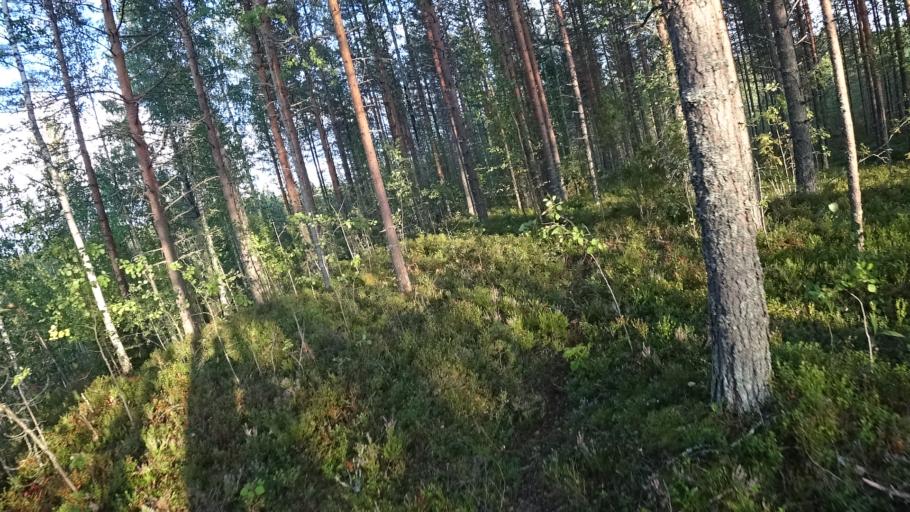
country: FI
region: North Karelia
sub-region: Joensuu
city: Ilomantsi
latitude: 62.6362
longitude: 31.0812
